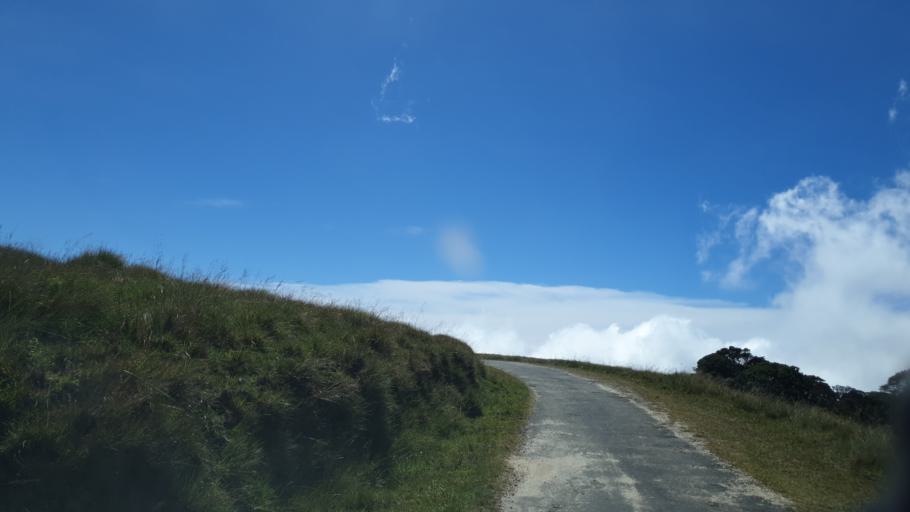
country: LK
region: Uva
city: Haputale
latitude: 6.7979
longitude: 80.8169
